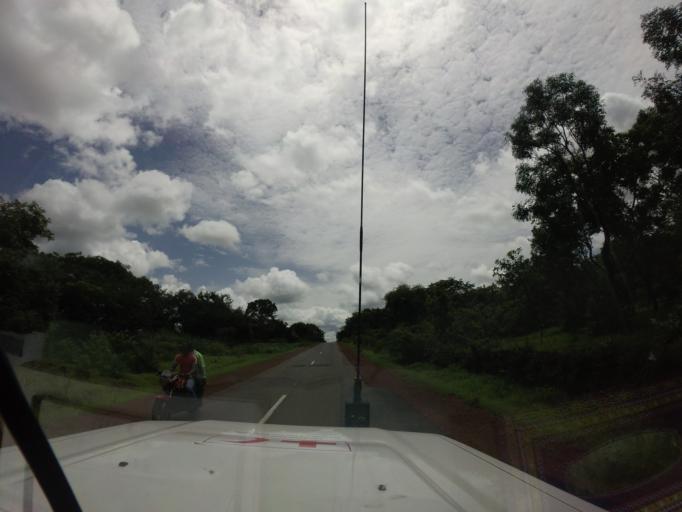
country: SL
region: Northern Province
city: Gberia Fotombu
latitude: 10.0977
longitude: -11.1444
